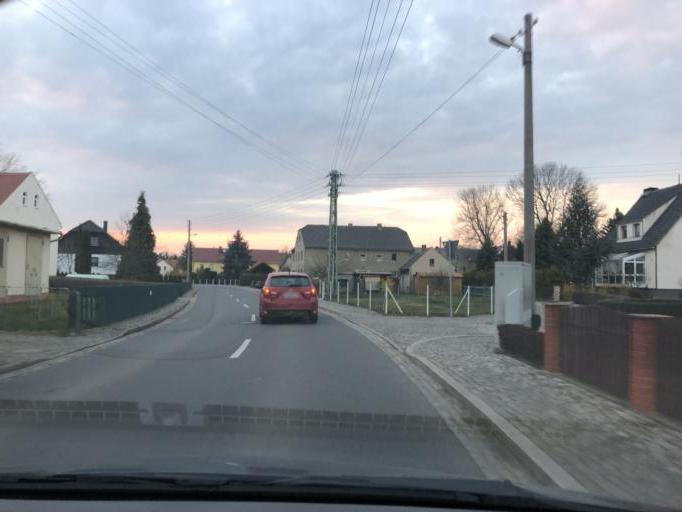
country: DE
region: Saxony
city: Haselbachtal
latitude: 51.2407
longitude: 14.0328
